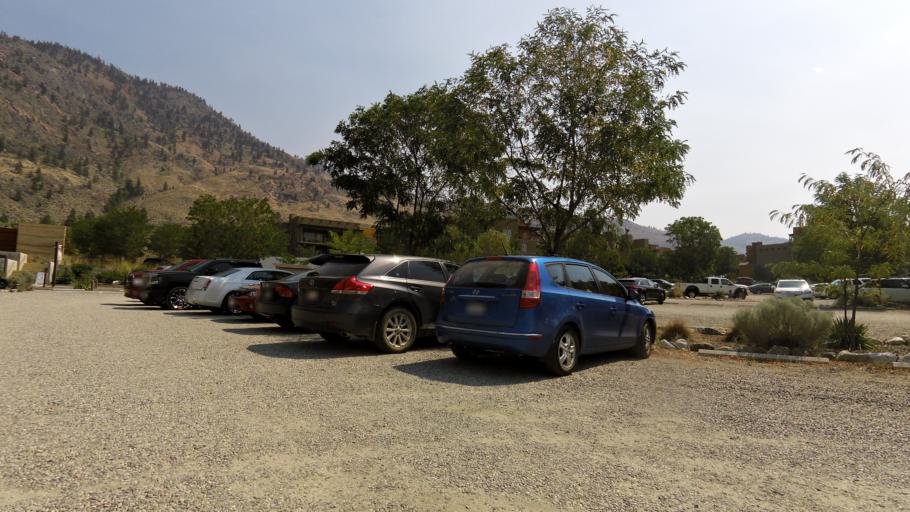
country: CA
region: British Columbia
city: Osoyoos
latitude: 49.0409
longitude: -119.4350
